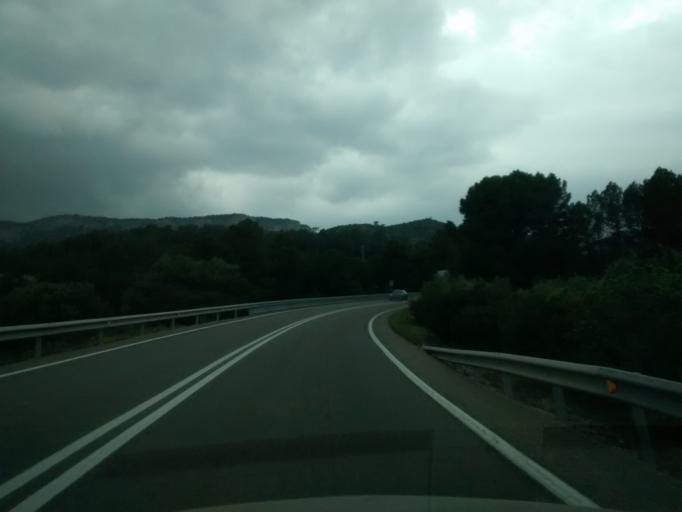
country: ES
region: Catalonia
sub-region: Provincia de Tarragona
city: Benifallet
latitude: 41.0224
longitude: 0.4989
